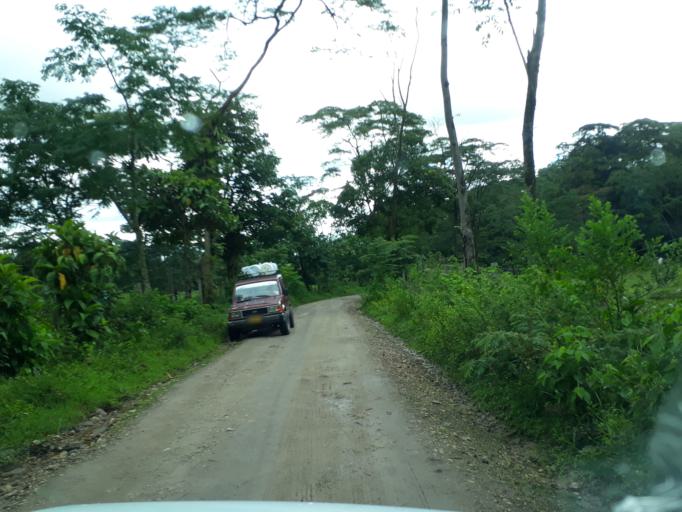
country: CO
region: Cundinamarca
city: Medina
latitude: 4.5811
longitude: -73.3788
